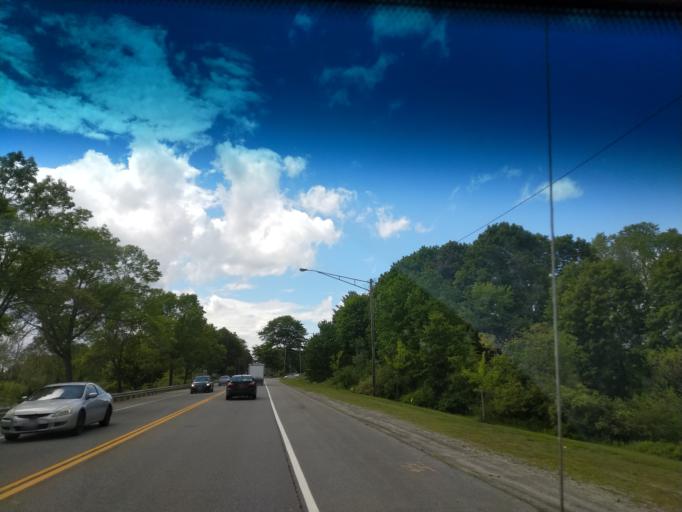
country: US
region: Maine
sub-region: Cumberland County
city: Westbrook
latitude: 43.6805
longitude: -70.3767
